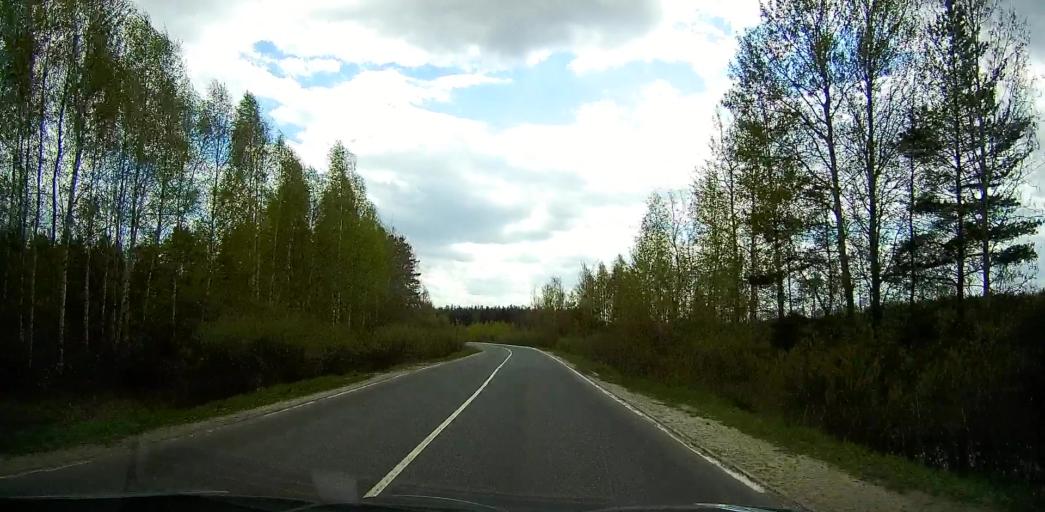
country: RU
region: Moskovskaya
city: Davydovo
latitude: 55.6600
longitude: 38.7544
